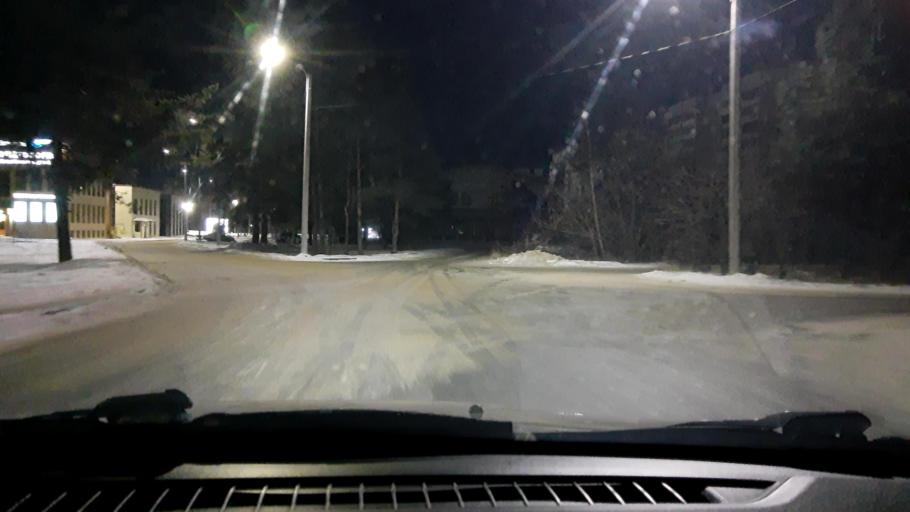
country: RU
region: Nizjnij Novgorod
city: Dzerzhinsk
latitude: 56.2277
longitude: 43.4124
